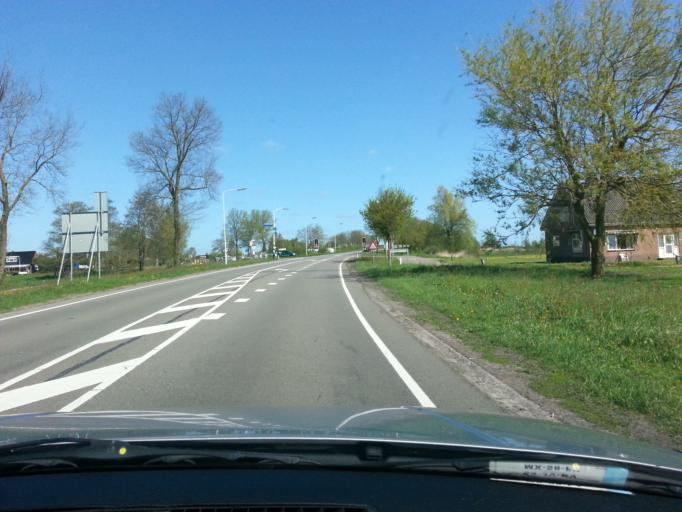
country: NL
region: Friesland
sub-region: Gemeente Achtkarspelen
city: Augustinusga
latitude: 53.2244
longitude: 6.1742
